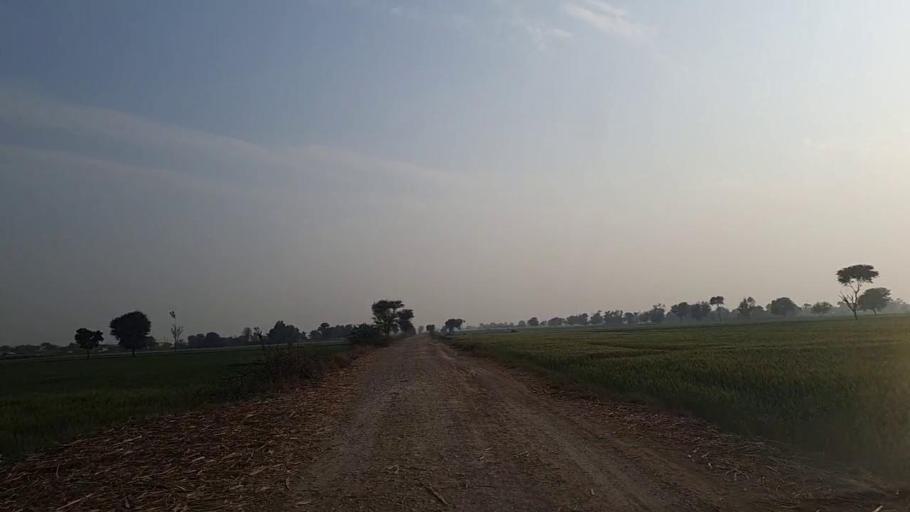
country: PK
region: Sindh
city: Jam Sahib
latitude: 26.3147
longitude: 68.5336
